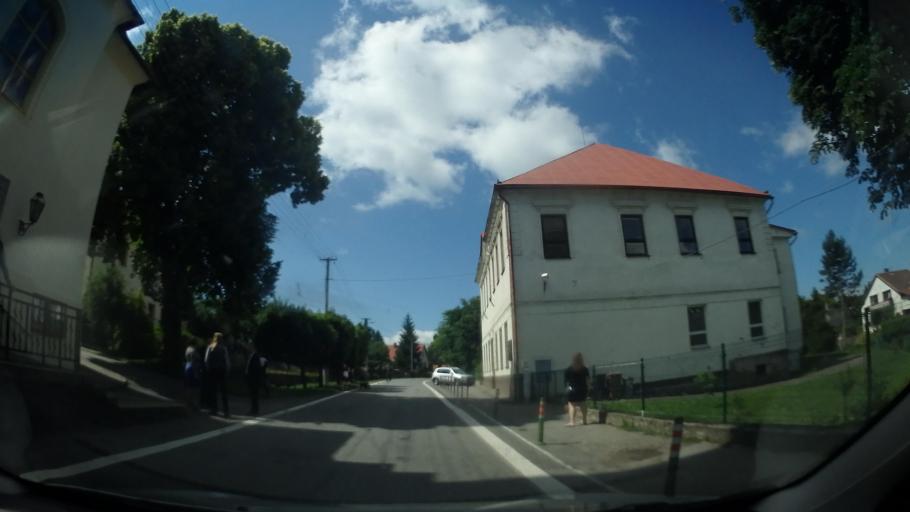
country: CZ
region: Vysocina
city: Heralec
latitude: 49.6284
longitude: 16.0385
